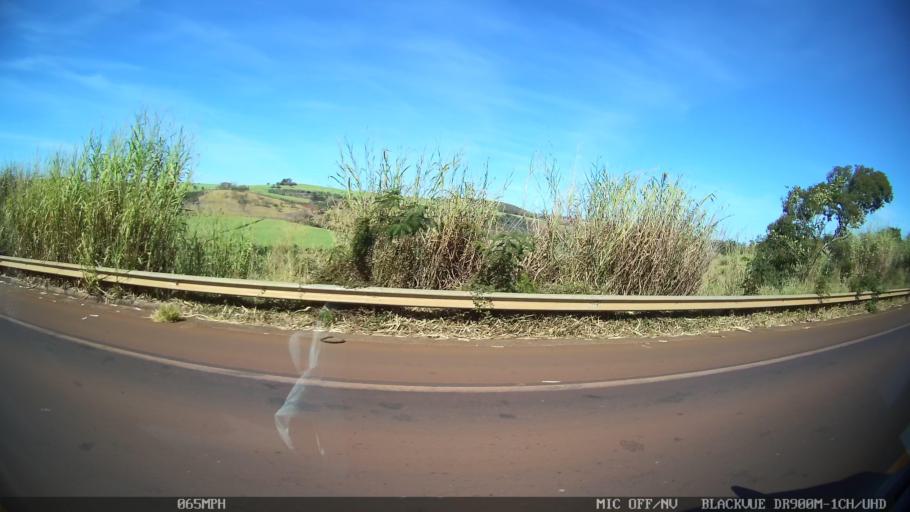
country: BR
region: Sao Paulo
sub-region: Sao Joaquim Da Barra
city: Sao Joaquim da Barra
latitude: -20.5545
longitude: -47.6804
